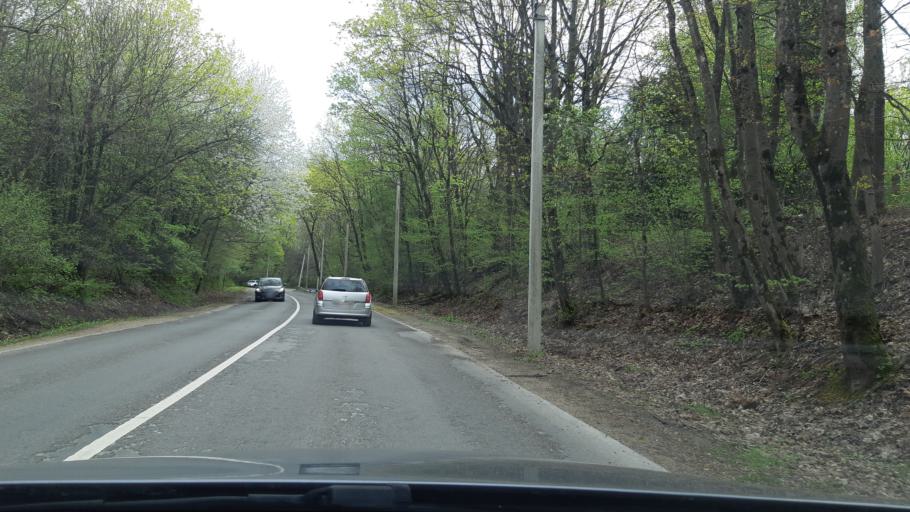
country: LT
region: Kauno apskritis
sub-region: Kaunas
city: Silainiai
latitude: 54.9241
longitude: 23.8565
